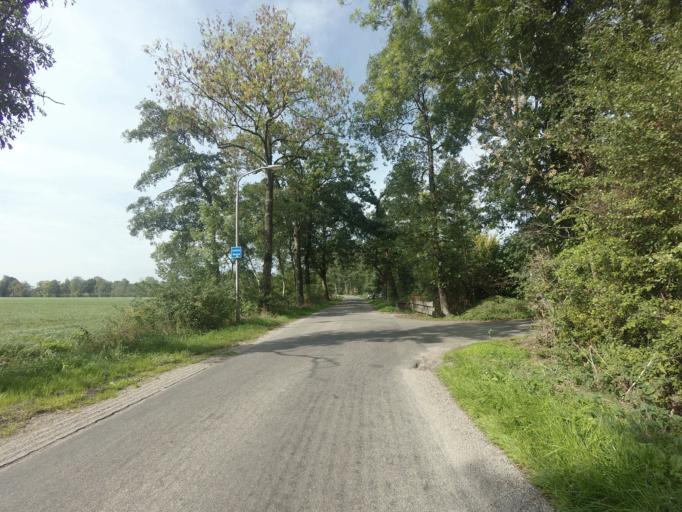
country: NL
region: Groningen
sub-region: Gemeente Zuidhorn
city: Grijpskerk
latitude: 53.2154
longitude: 6.3389
